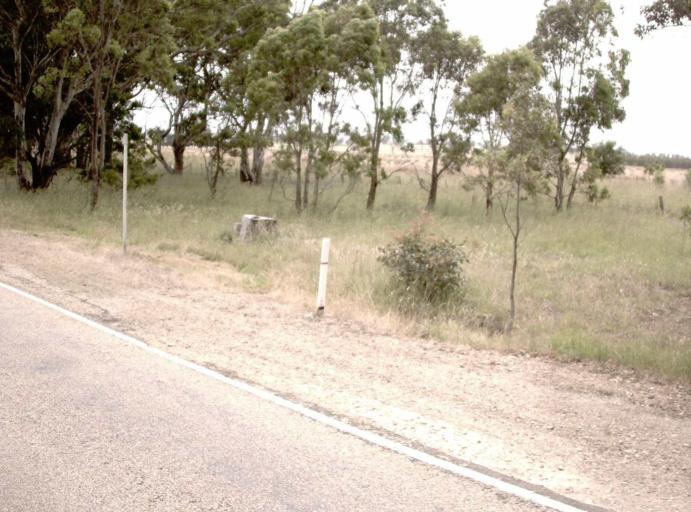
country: AU
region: Victoria
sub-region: Wellington
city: Sale
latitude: -37.9350
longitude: 147.0961
